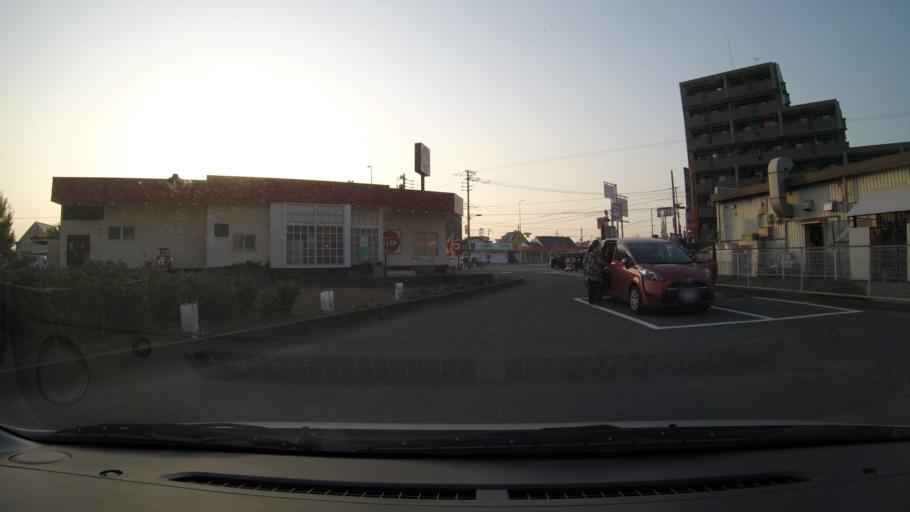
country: JP
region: Fukuoka
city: Fukuoka-shi
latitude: 33.6323
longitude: 130.4625
